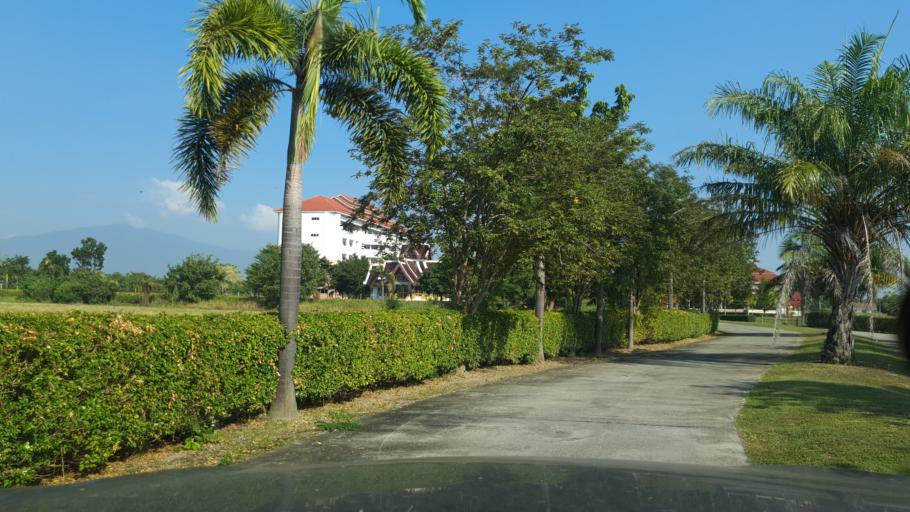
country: TH
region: Chiang Mai
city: Hang Dong
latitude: 18.7097
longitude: 98.9751
